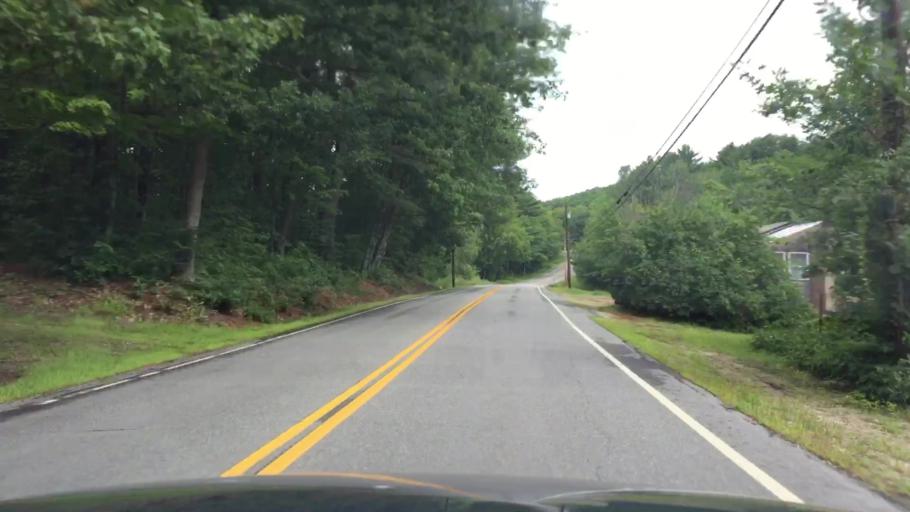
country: US
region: New Hampshire
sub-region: Carroll County
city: Center Harbor
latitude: 43.7427
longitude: -71.4780
